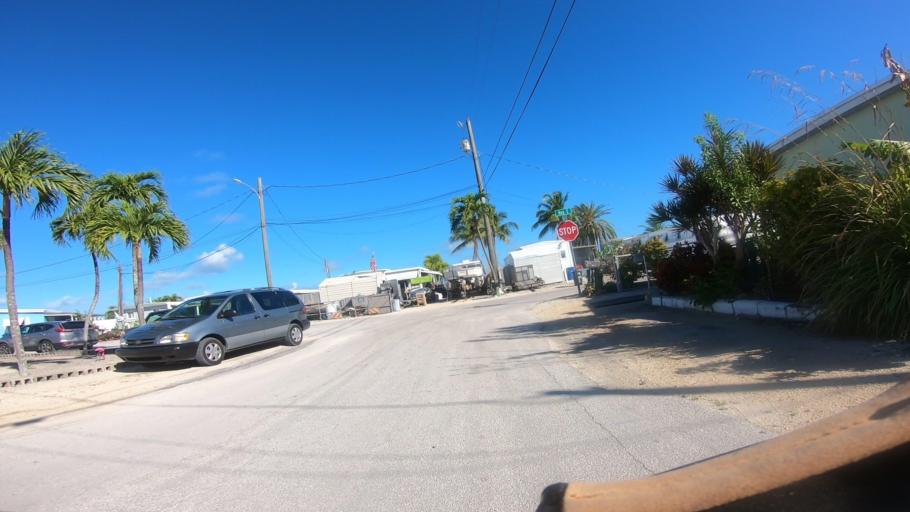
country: US
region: Florida
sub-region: Monroe County
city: Key Largo
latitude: 25.1156
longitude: -80.4249
